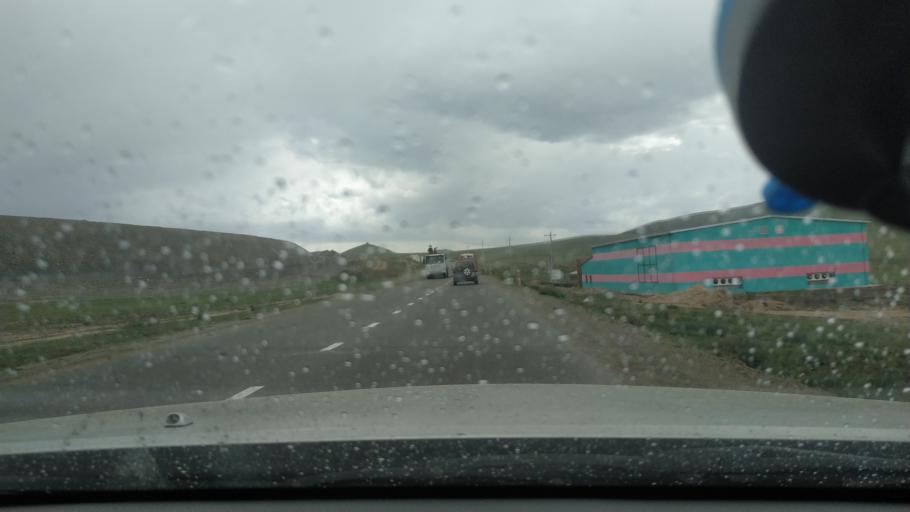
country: MN
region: Ulaanbaatar
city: Ulaanbaatar
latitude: 47.7965
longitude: 106.7455
